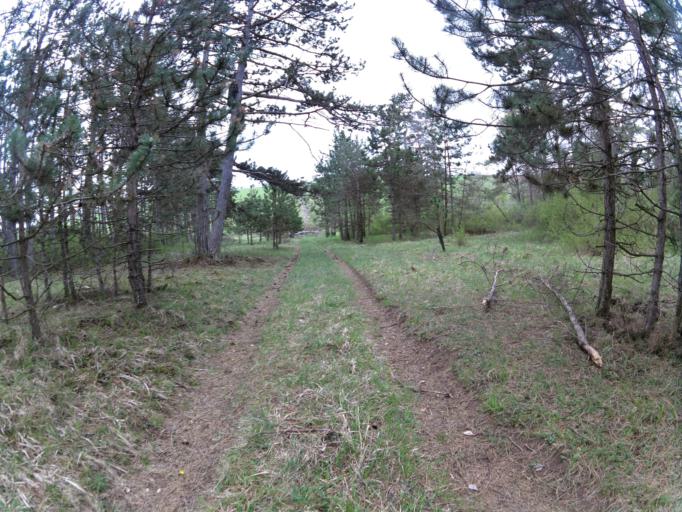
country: DE
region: Bavaria
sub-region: Regierungsbezirk Unterfranken
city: Greussenheim
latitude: 49.8334
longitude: 9.7925
